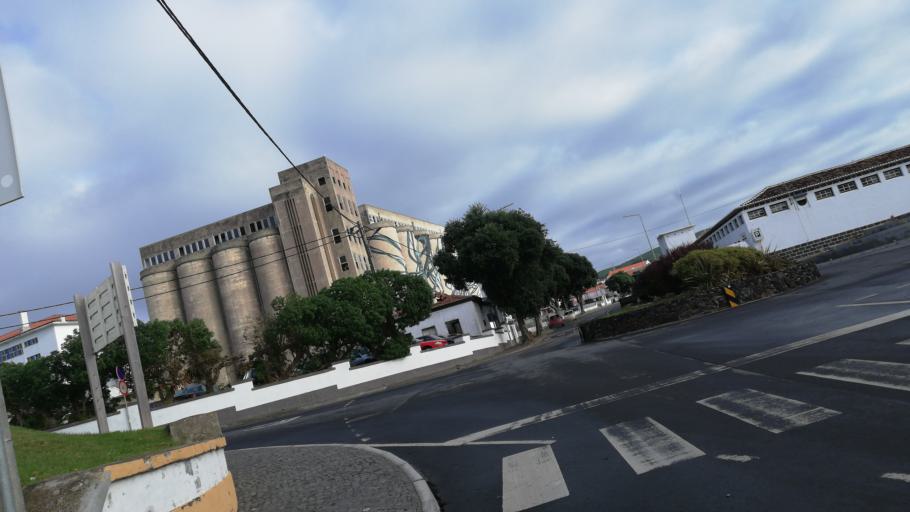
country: PT
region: Azores
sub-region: Angra do Heroismo
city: Angra do Heroismo
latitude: 38.6539
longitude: -27.2130
